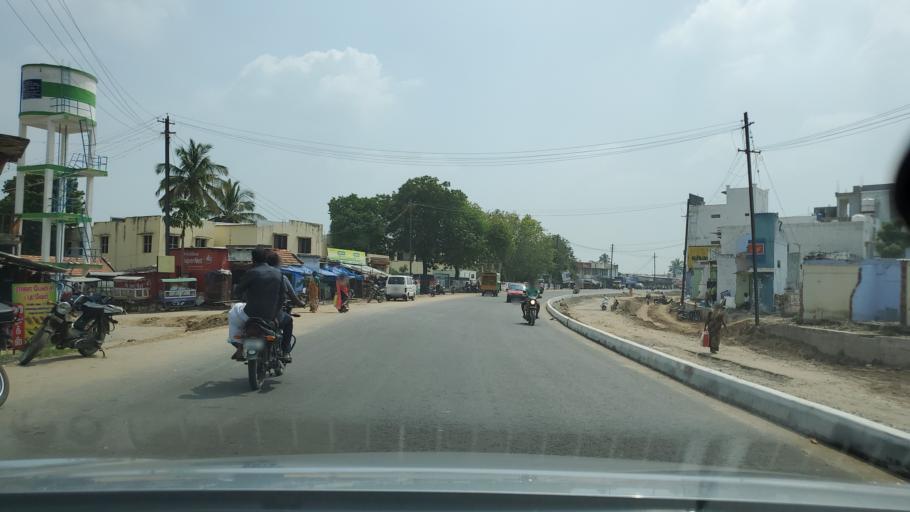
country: IN
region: Tamil Nadu
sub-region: Tiruppur
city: Kangayam
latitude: 10.9429
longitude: 77.4375
